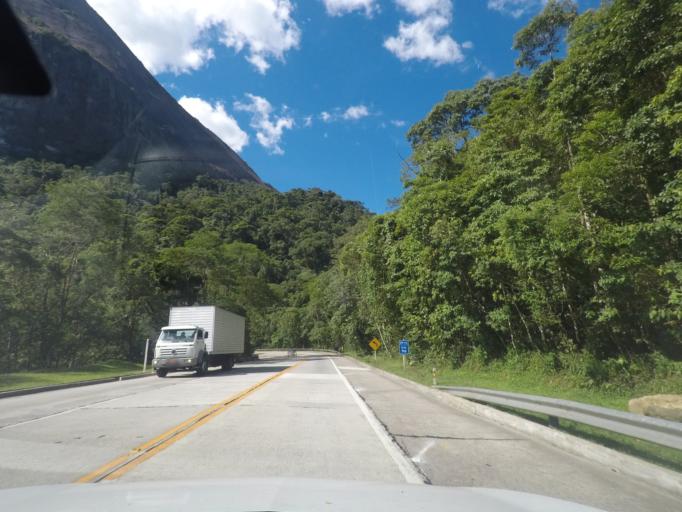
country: BR
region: Rio de Janeiro
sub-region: Guapimirim
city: Guapimirim
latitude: -22.4870
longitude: -42.9995
